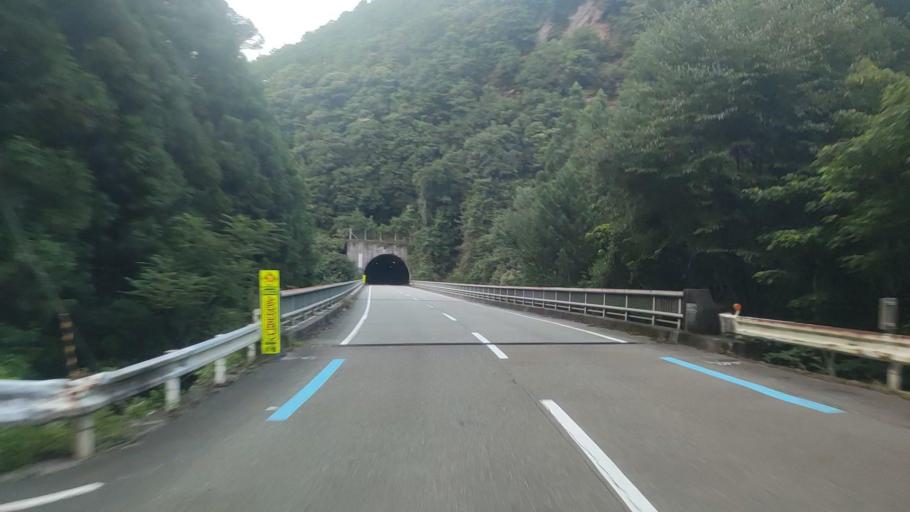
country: JP
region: Wakayama
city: Shingu
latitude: 33.8079
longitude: 135.7211
